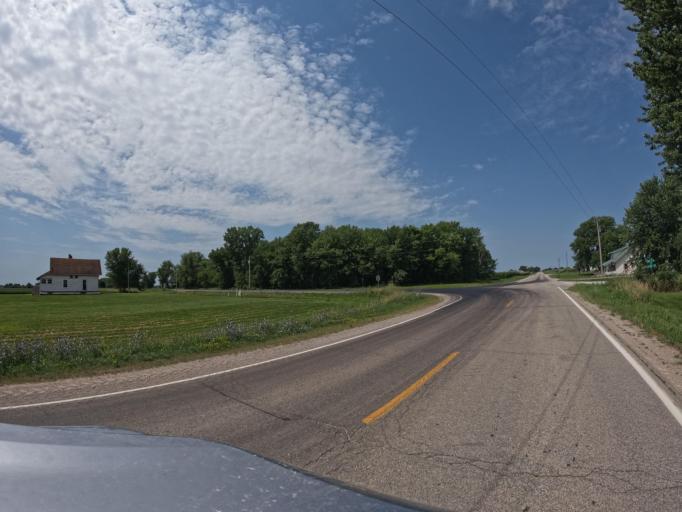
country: US
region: Iowa
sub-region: Appanoose County
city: Centerville
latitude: 40.8123
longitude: -92.9444
